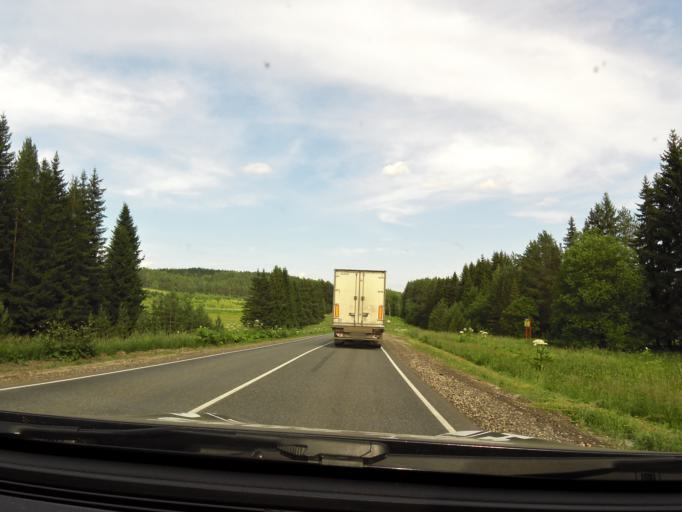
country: RU
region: Kirov
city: Slobodskoy
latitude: 58.7633
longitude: 50.3350
